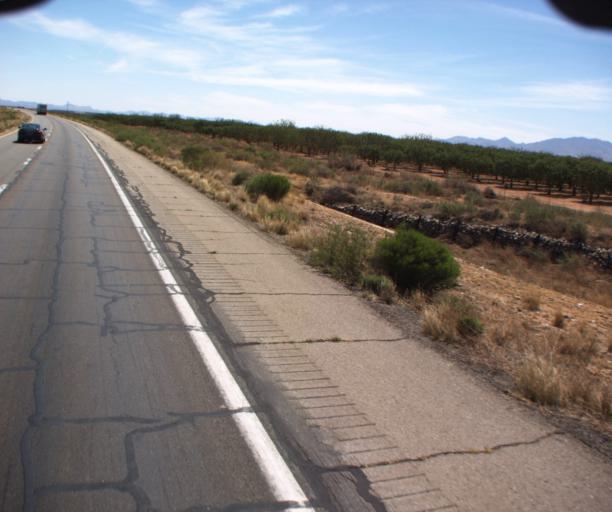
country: US
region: Arizona
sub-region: Cochise County
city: Willcox
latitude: 32.3177
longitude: -109.4905
